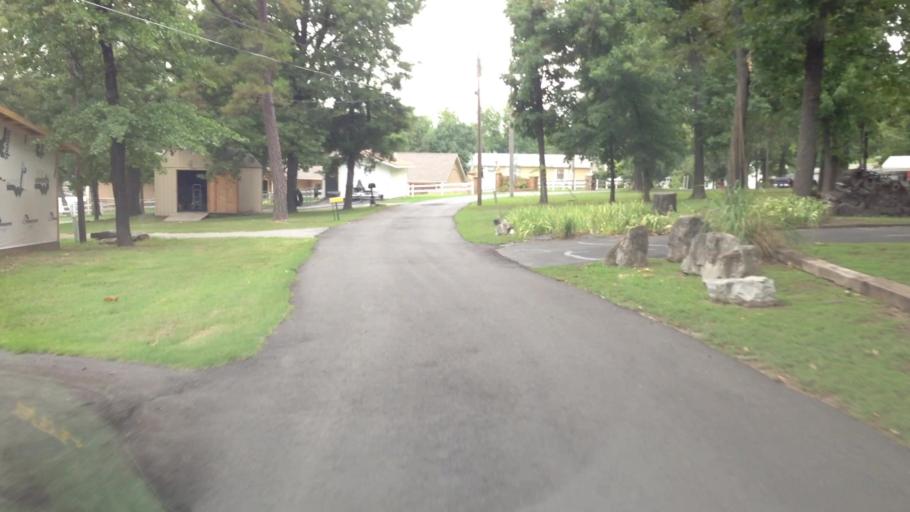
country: US
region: Oklahoma
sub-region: Delaware County
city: Cleora
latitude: 36.5496
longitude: -94.9671
